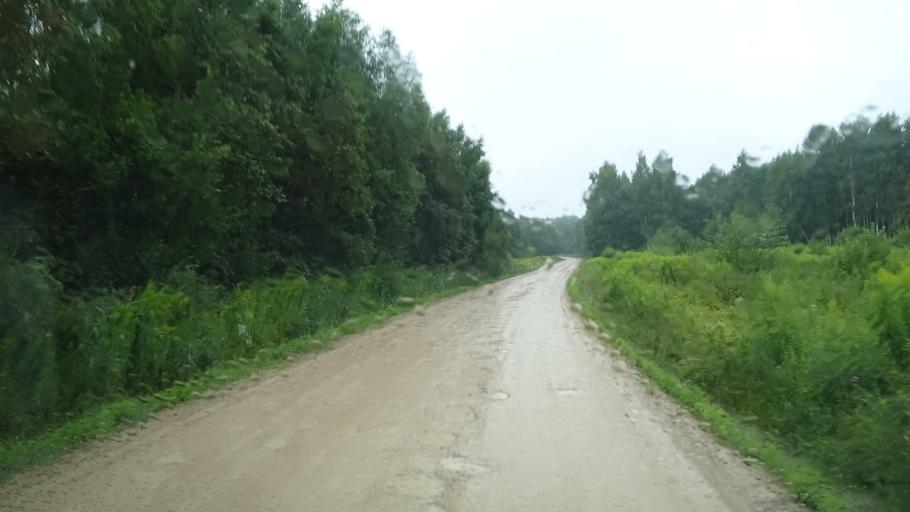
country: LV
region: Lecava
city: Iecava
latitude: 56.6633
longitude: 24.1678
